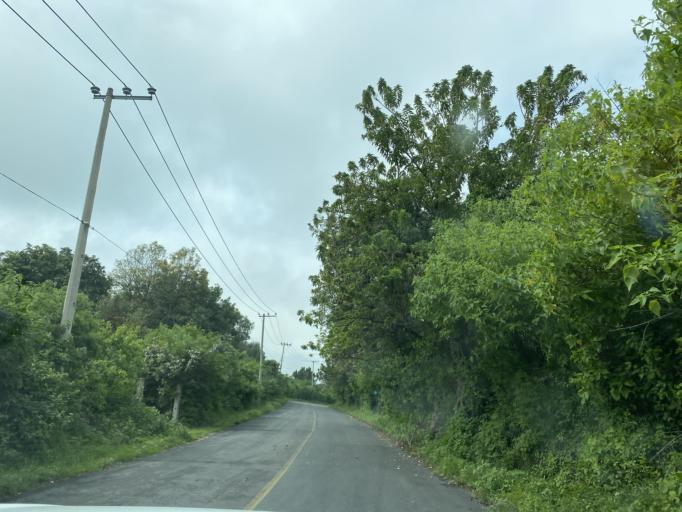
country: MX
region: Mexico
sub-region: Ozumba
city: San Jose Tlacotitlan
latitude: 18.9962
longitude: -98.8028
